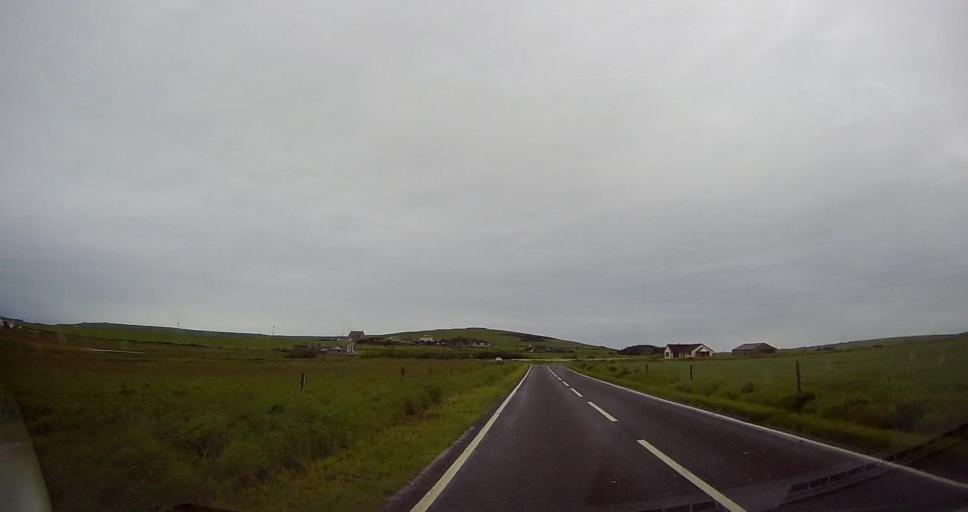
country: GB
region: Scotland
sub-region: Orkney Islands
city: Stromness
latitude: 59.0958
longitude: -3.2665
